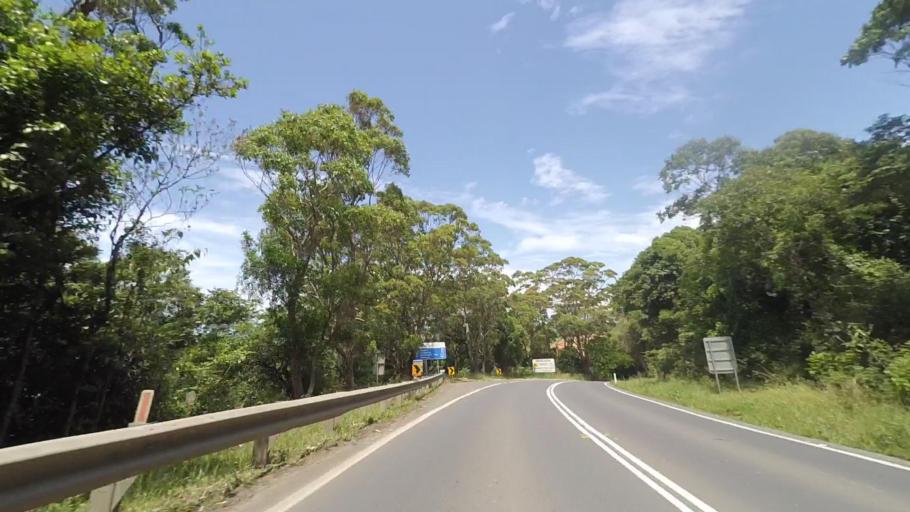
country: AU
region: New South Wales
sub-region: Shoalhaven Shire
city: Berry
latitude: -34.7526
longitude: 150.7500
